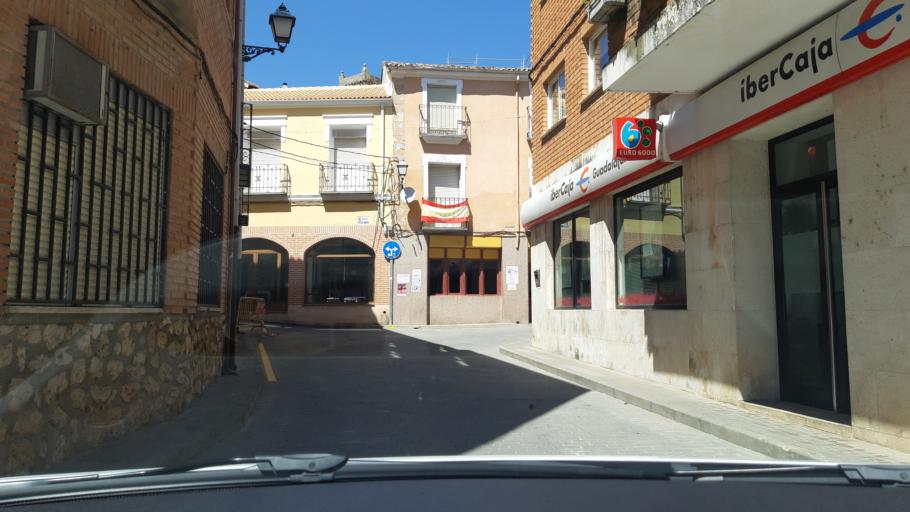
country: ES
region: Castille-La Mancha
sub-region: Provincia de Guadalajara
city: Cifuentes
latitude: 40.7849
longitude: -2.6220
